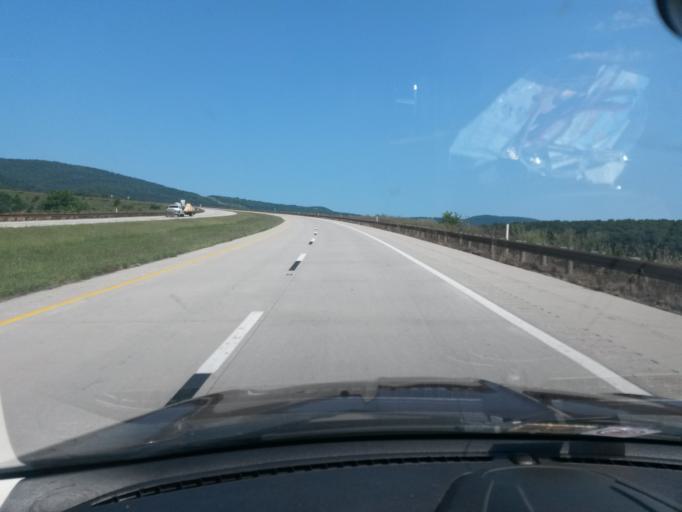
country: US
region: West Virginia
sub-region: Hardy County
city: Moorefield
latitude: 39.1430
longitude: -78.9808
